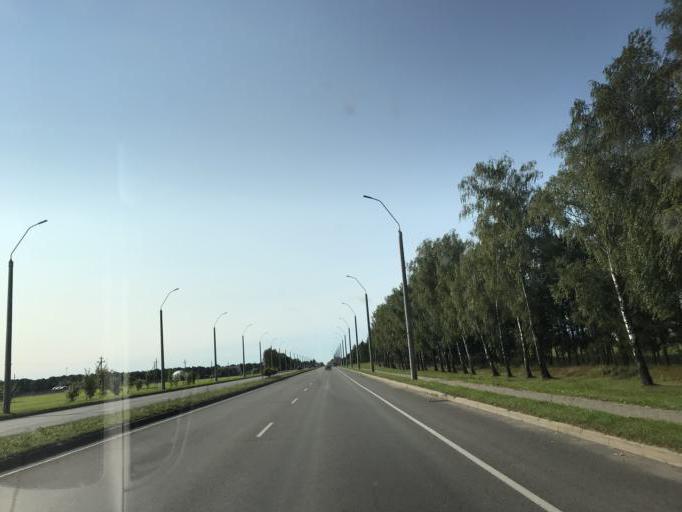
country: BY
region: Mogilev
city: Buynichy
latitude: 53.8688
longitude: 30.2614
